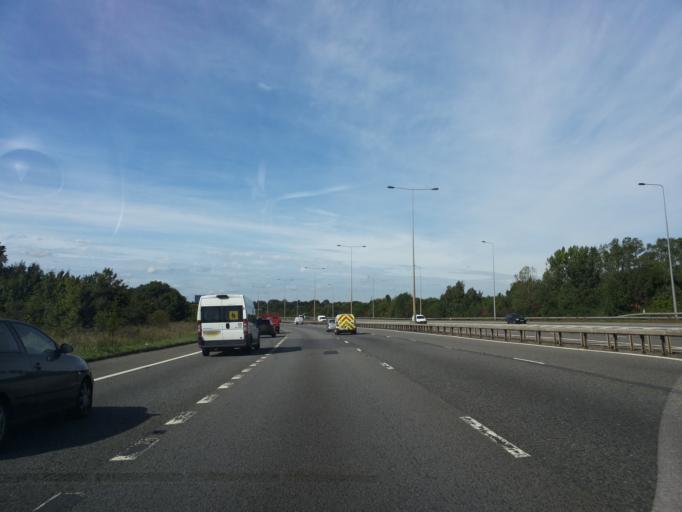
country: GB
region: England
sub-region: Kent
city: Boxley
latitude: 51.2968
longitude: 0.5254
